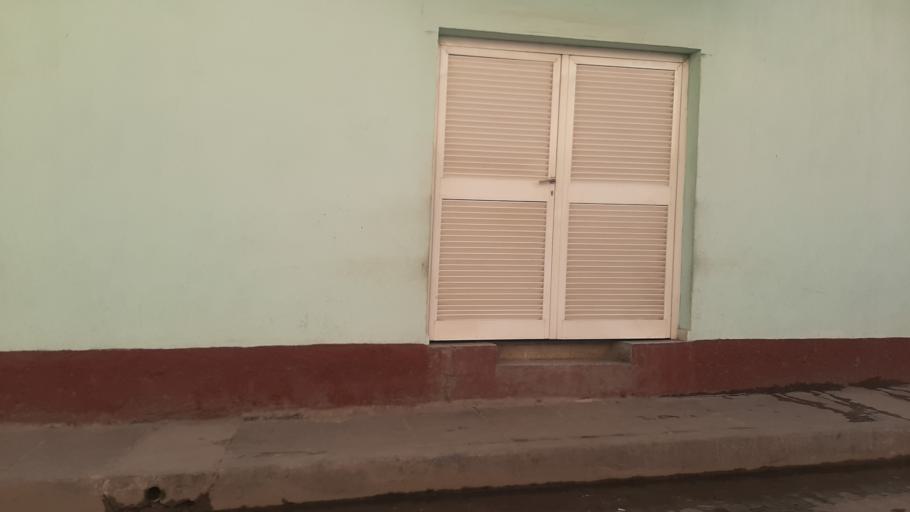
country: CU
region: Villa Clara
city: Santa Clara
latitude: 22.4090
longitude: -79.9628
